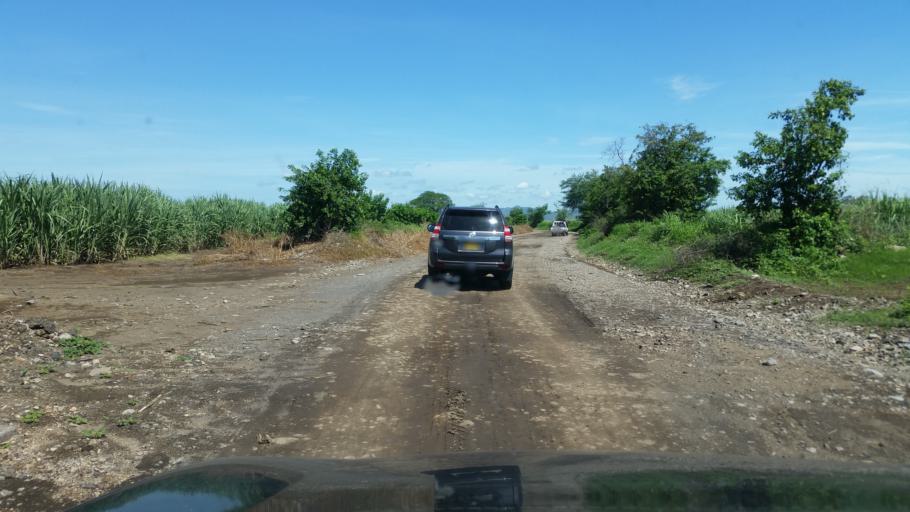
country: NI
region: Chinandega
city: Puerto Morazan
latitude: 12.7736
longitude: -87.1006
